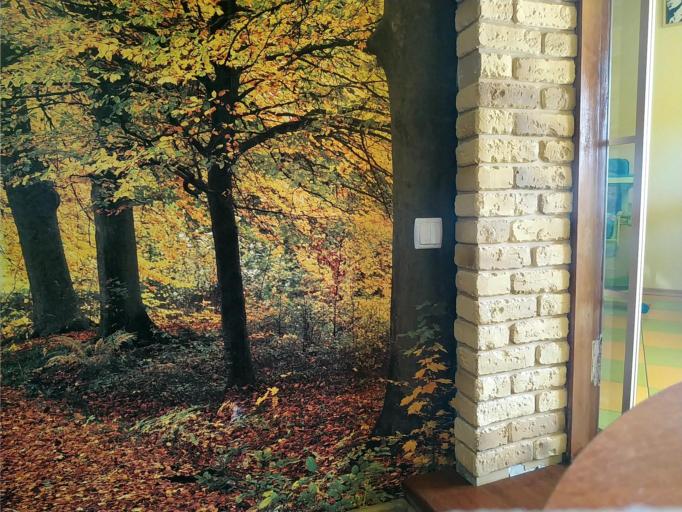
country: RU
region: Smolensk
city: Katyn'
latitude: 54.9820
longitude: 31.7283
